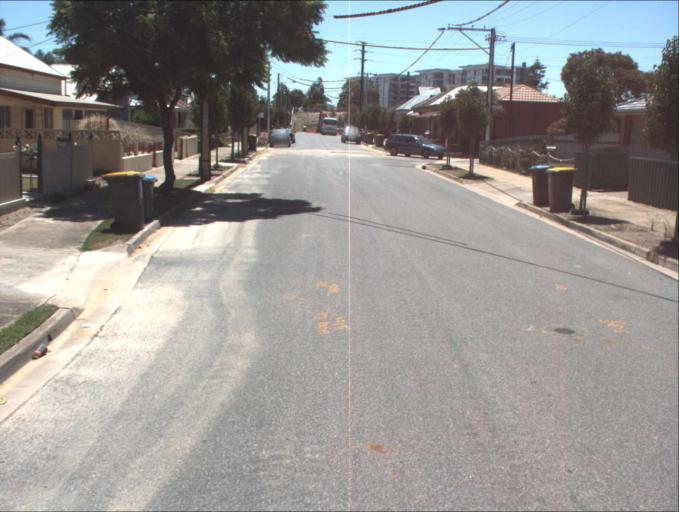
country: AU
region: South Australia
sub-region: Charles Sturt
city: West Lakes Shore
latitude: -34.8484
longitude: 138.4930
